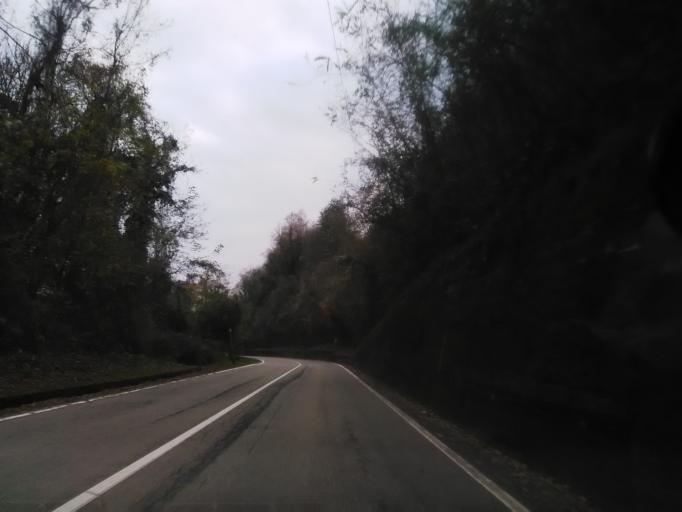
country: IT
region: Piedmont
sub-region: Provincia di Vercelli
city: Quarona
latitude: 45.7775
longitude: 8.2595
